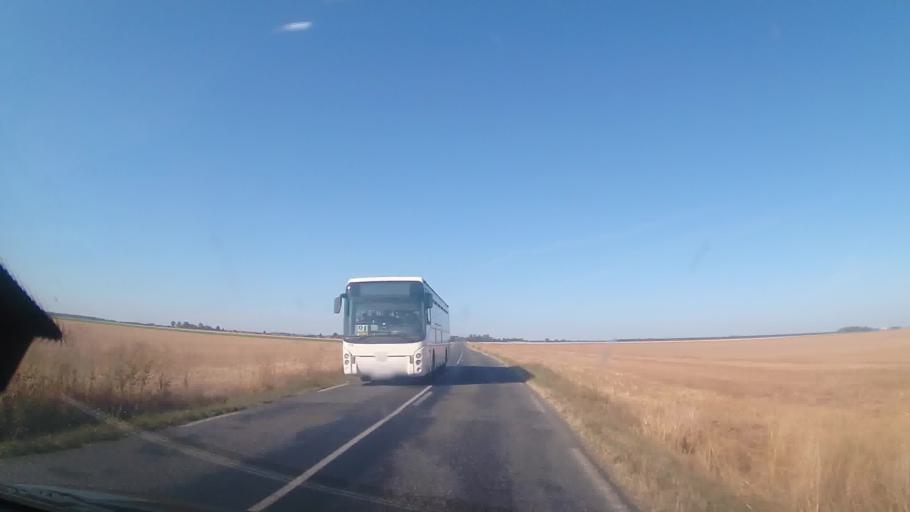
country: FR
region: Ile-de-France
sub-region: Departement de l'Essonne
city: Corbreuse
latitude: 48.4574
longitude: 1.9292
